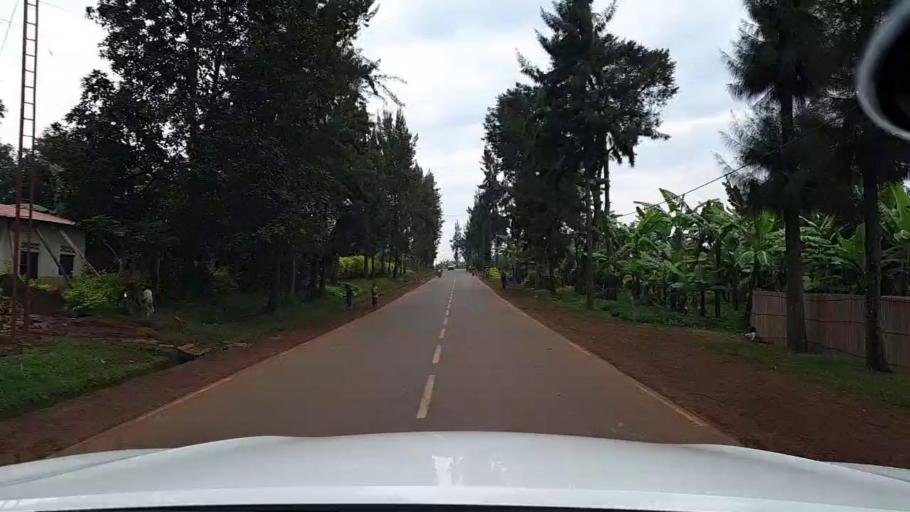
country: RW
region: Western Province
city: Cyangugu
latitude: -2.6160
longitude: 28.9444
